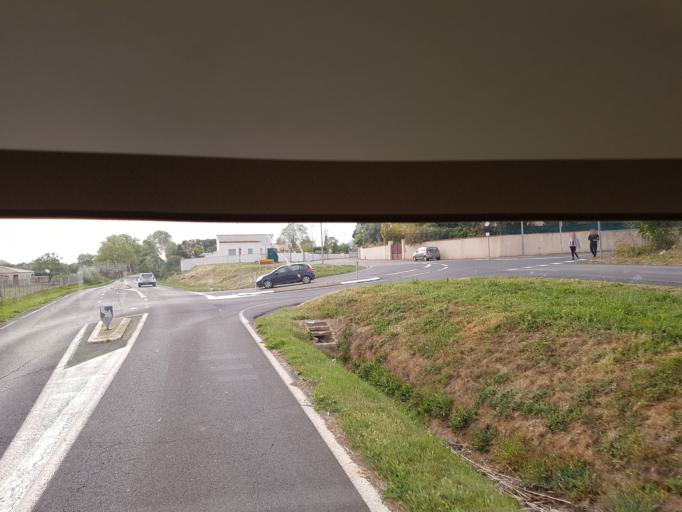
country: FR
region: Languedoc-Roussillon
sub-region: Departement de l'Herault
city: Florensac
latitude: 43.3787
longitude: 3.4767
